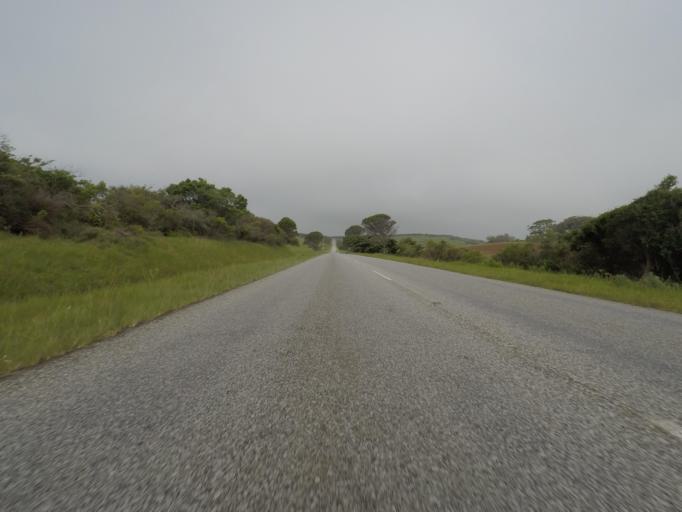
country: ZA
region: Eastern Cape
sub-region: Cacadu District Municipality
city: Port Alfred
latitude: -33.6060
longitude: 26.8298
